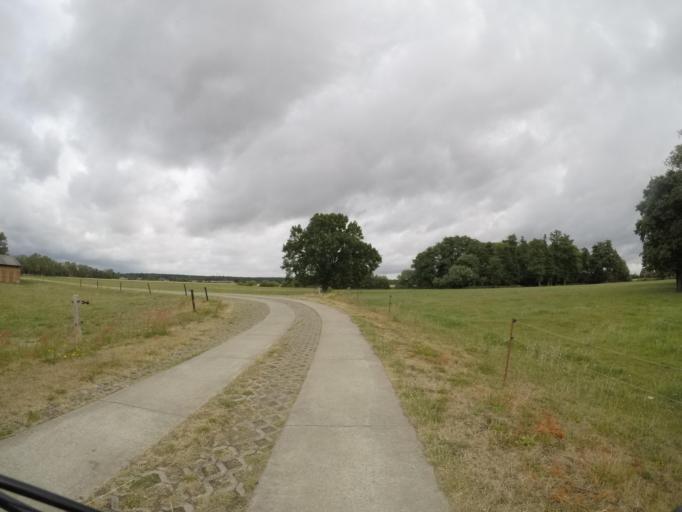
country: DE
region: Lower Saxony
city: Hitzacker
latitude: 53.1740
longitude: 11.1140
